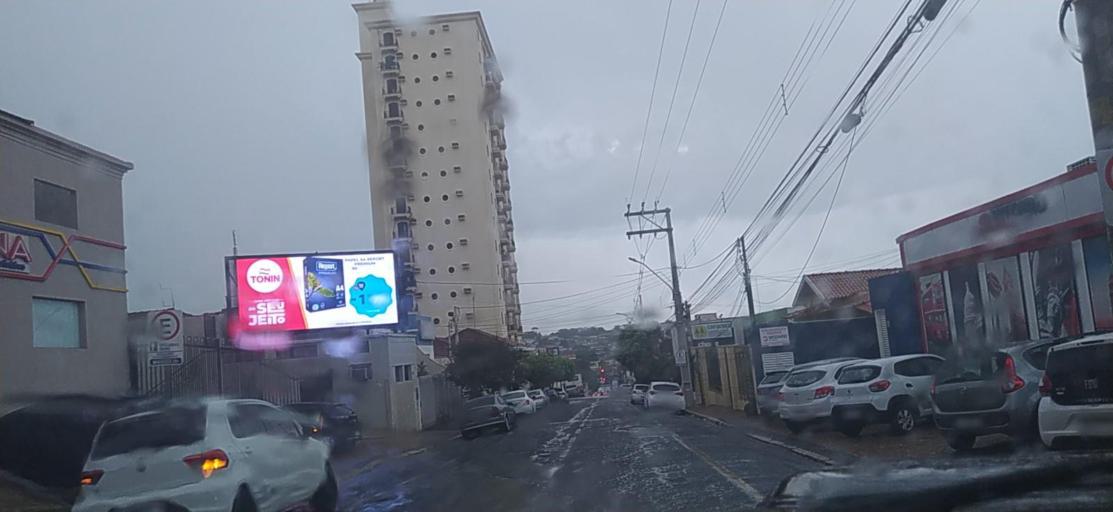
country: BR
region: Sao Paulo
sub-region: Catanduva
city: Catanduva
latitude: -21.1374
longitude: -48.9710
